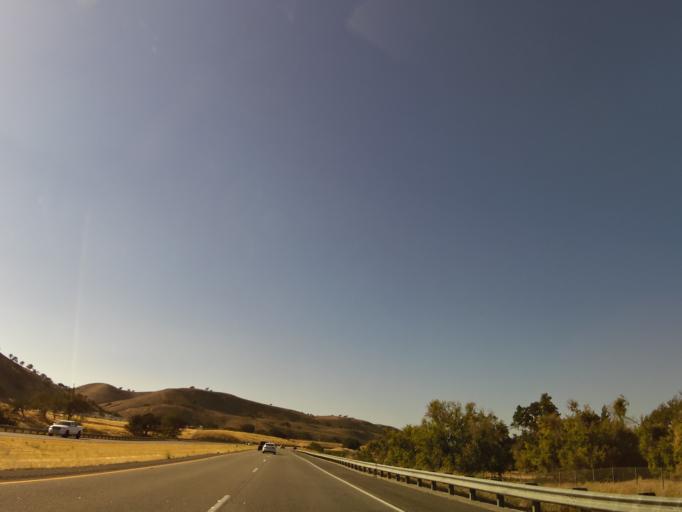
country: US
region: California
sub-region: San Luis Obispo County
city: San Miguel
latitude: 35.8209
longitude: -120.7578
